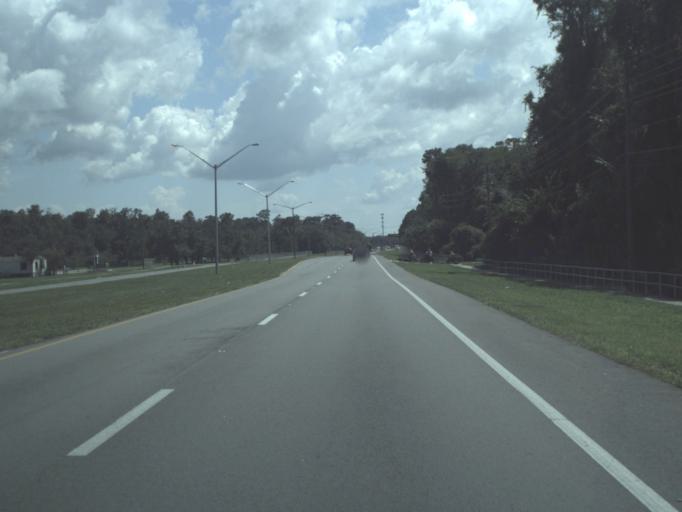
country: US
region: Florida
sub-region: Pasco County
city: Trinity
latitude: 28.1573
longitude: -82.6967
